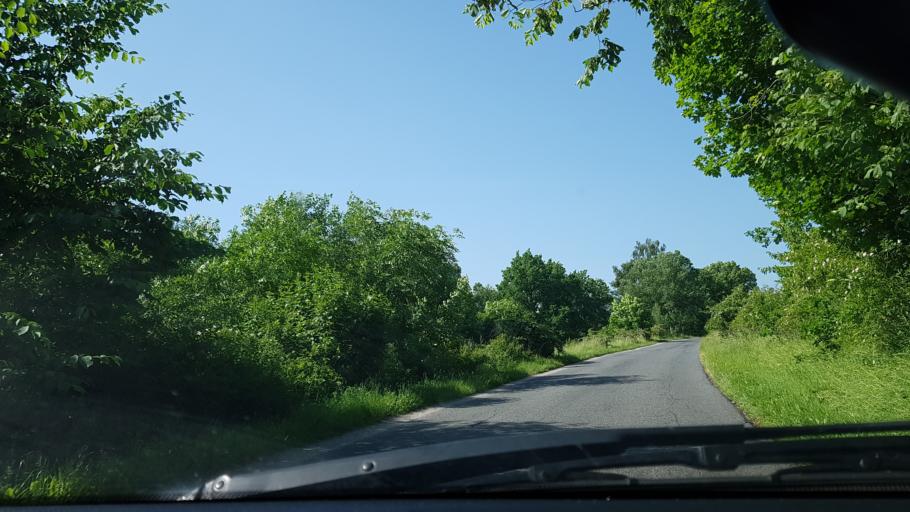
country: PL
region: Lower Silesian Voivodeship
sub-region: Powiat klodzki
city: Bozkow
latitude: 50.5137
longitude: 16.6448
